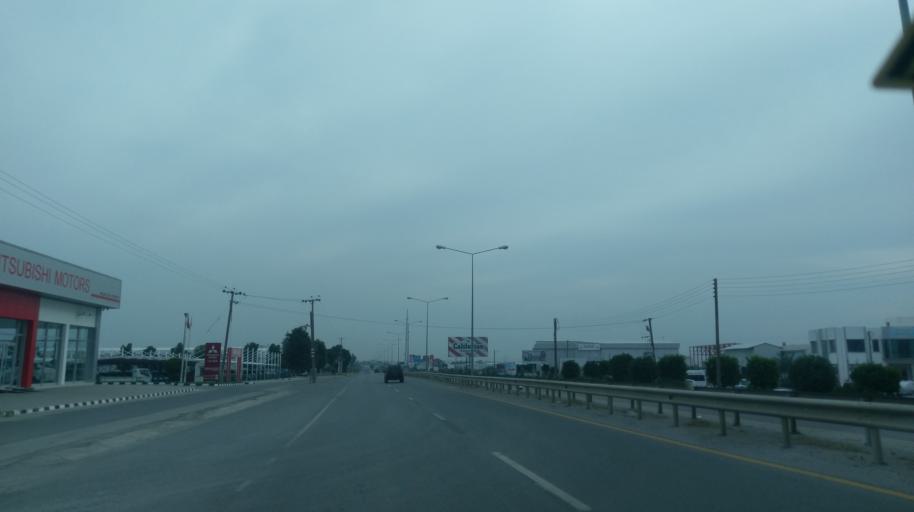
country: CY
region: Lefkosia
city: Mammari
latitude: 35.2127
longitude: 33.2644
